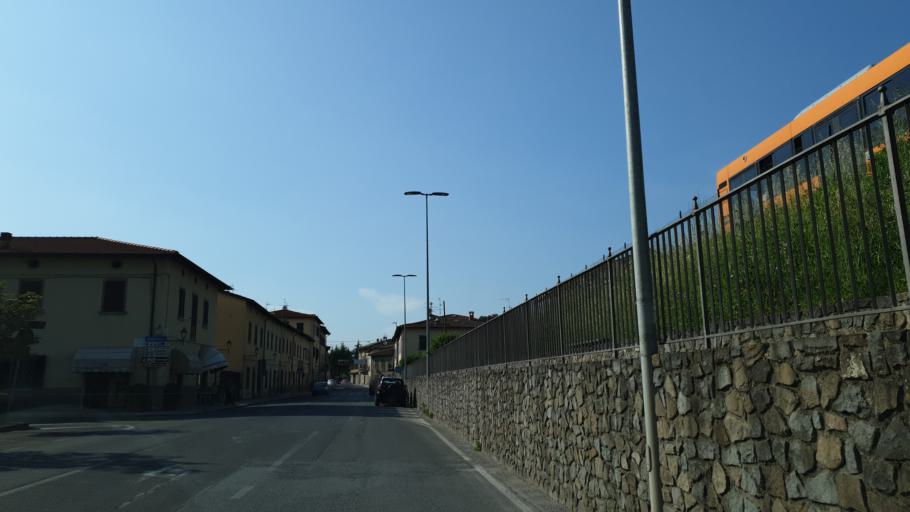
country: IT
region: Tuscany
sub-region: Province of Arezzo
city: Ponte a Poppi
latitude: 43.7303
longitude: 11.7676
